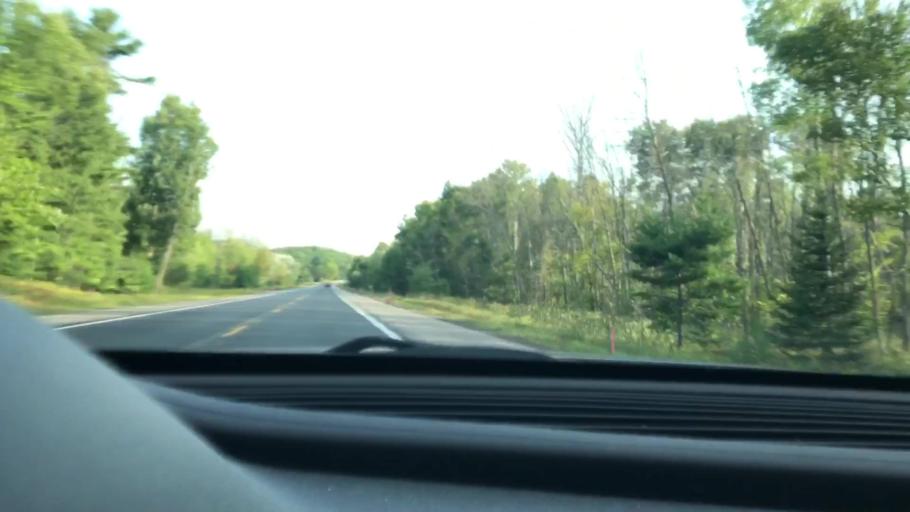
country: US
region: Michigan
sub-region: Antrim County
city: Bellaire
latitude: 45.1161
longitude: -85.3503
